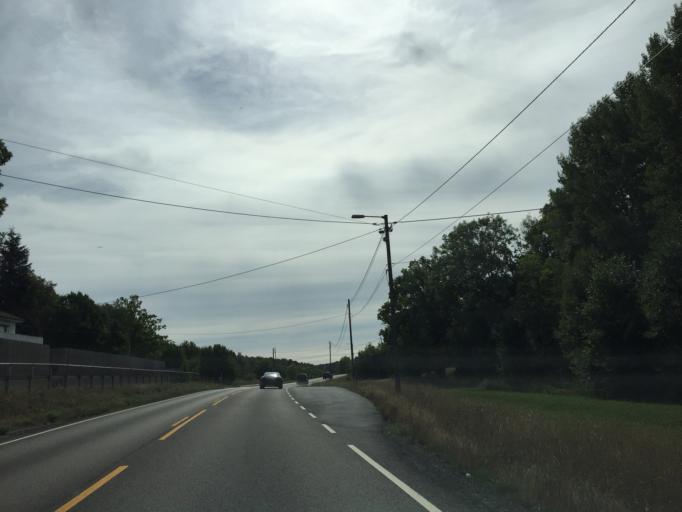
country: NO
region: Ostfold
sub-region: Fredrikstad
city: Fredrikstad
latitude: 59.1769
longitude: 10.9314
